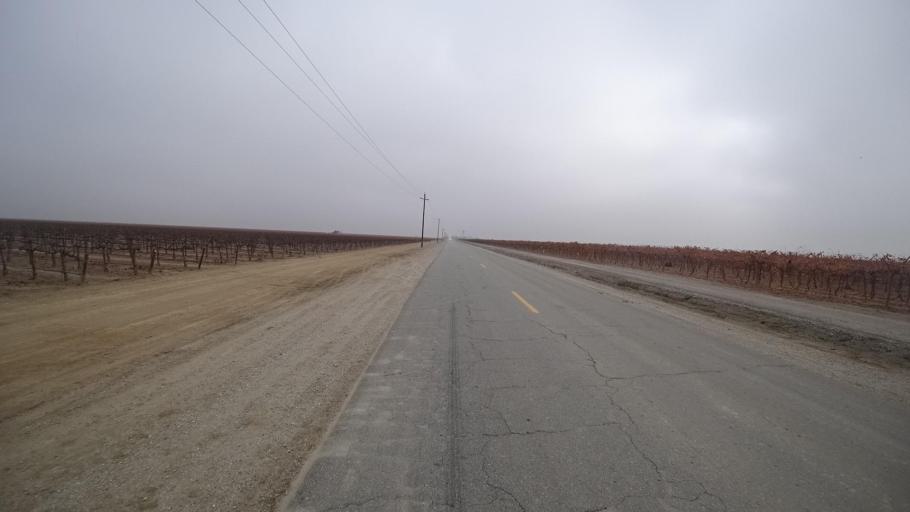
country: US
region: California
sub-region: Kern County
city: Maricopa
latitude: 35.0940
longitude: -119.1981
